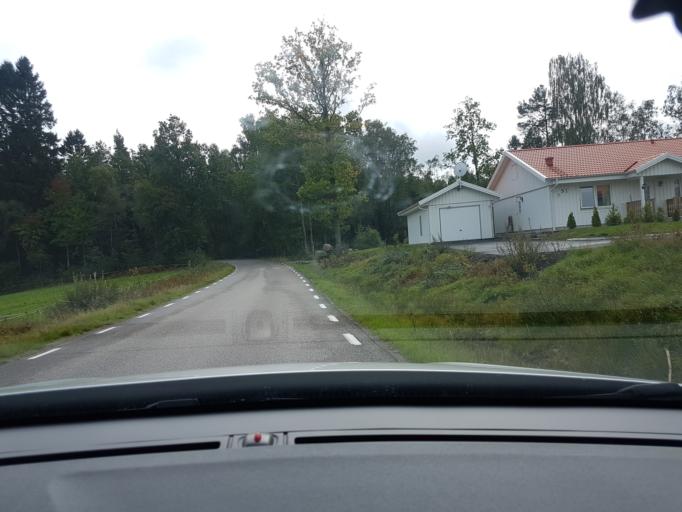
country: SE
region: Vaestra Goetaland
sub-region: Ale Kommun
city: Alvangen
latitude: 57.9110
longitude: 12.1566
